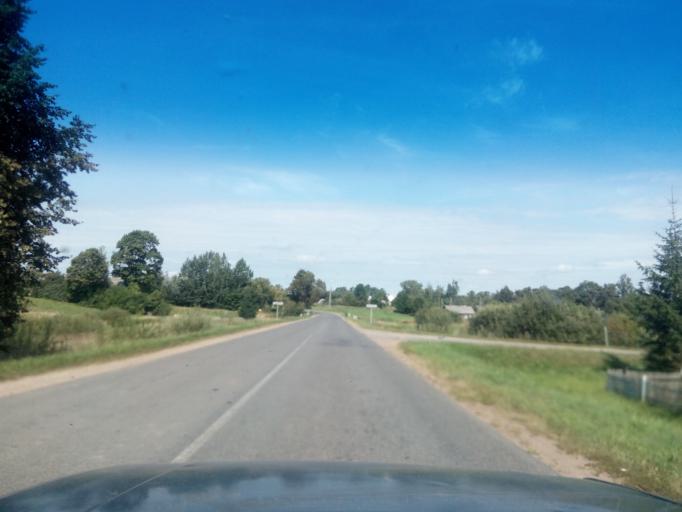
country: BY
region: Vitebsk
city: Vyerkhnyadzvinsk
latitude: 55.8295
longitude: 27.7357
